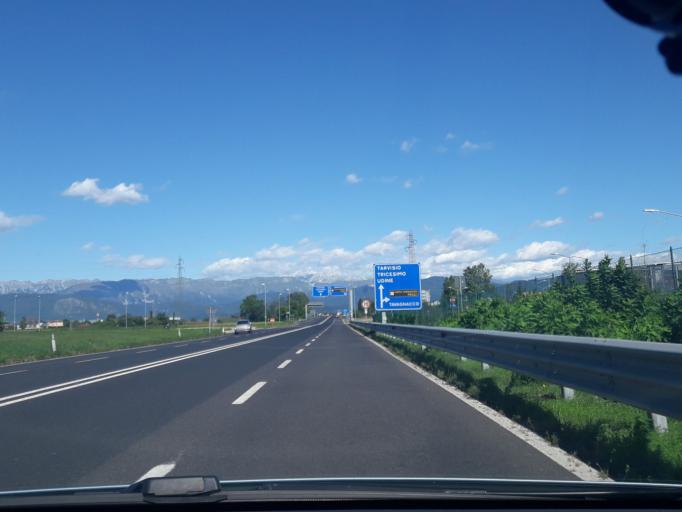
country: IT
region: Friuli Venezia Giulia
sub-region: Provincia di Udine
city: Tavagnacco
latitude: 46.1162
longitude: 13.2192
